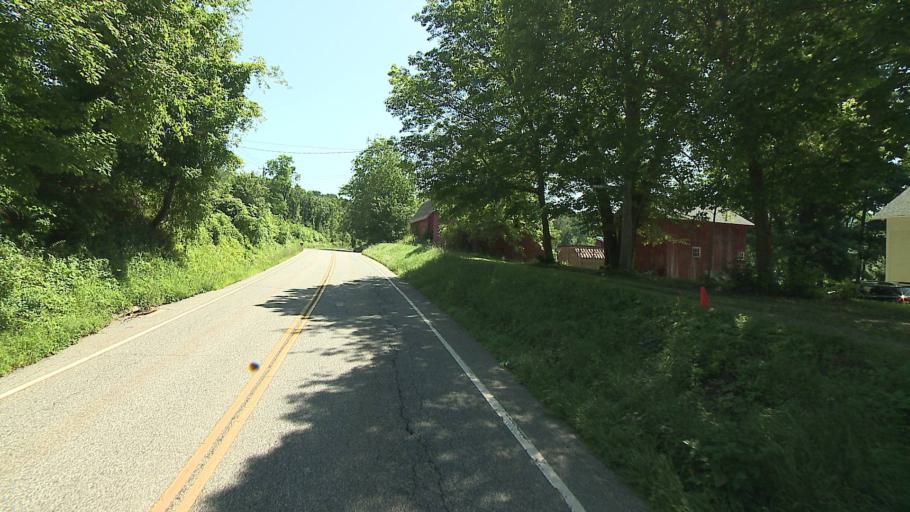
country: US
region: Connecticut
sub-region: Litchfield County
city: Kent
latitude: 41.8549
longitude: -73.4501
